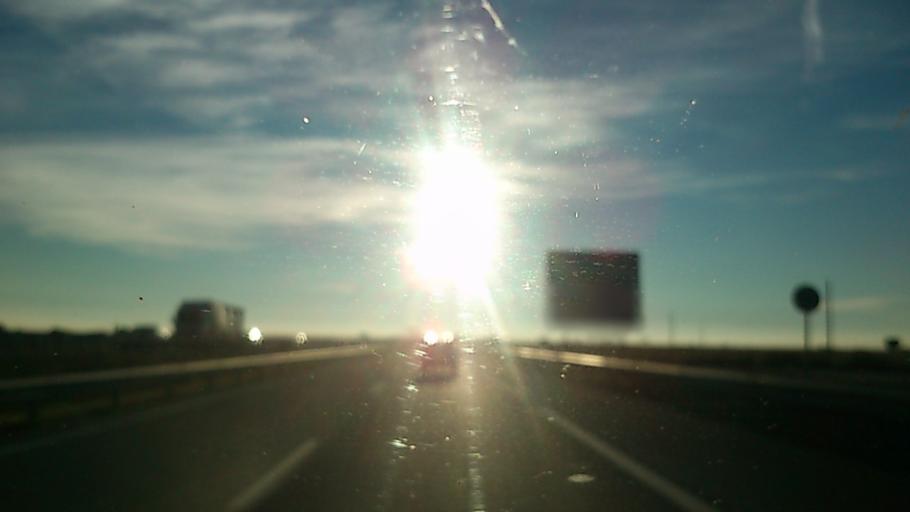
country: ES
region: Castille-La Mancha
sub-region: Provincia de Guadalajara
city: Muduex
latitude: 40.8152
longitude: -2.9329
